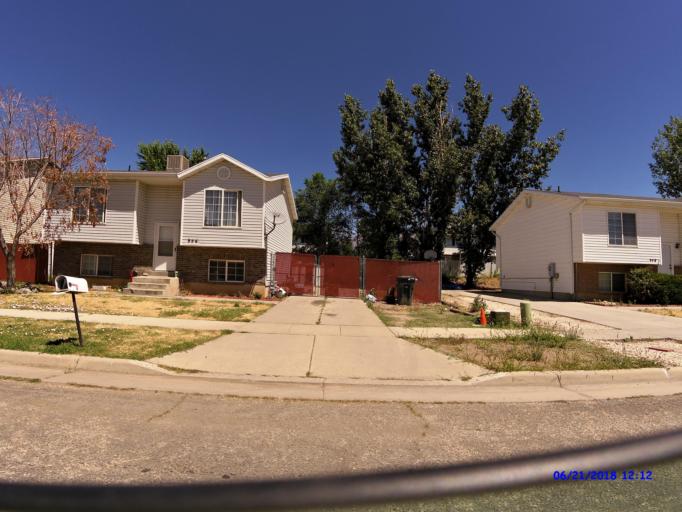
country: US
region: Utah
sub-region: Weber County
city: Harrisville
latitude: 41.2851
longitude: -112.0025
